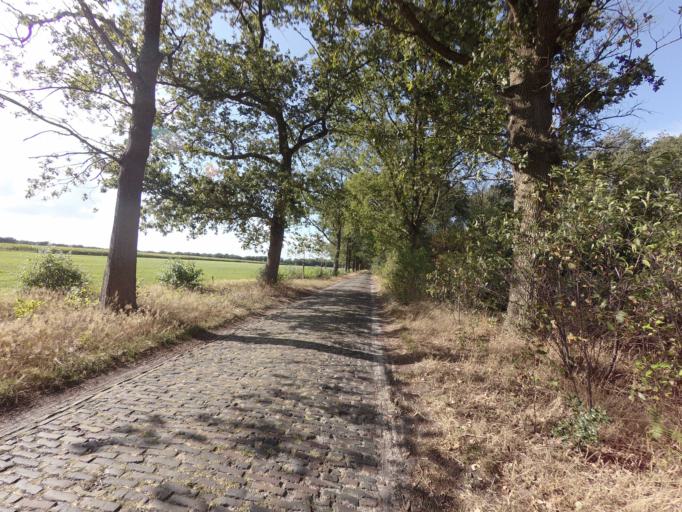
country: NL
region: Friesland
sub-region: Gemeente Heerenveen
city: Jubbega
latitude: 52.9573
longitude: 6.1828
